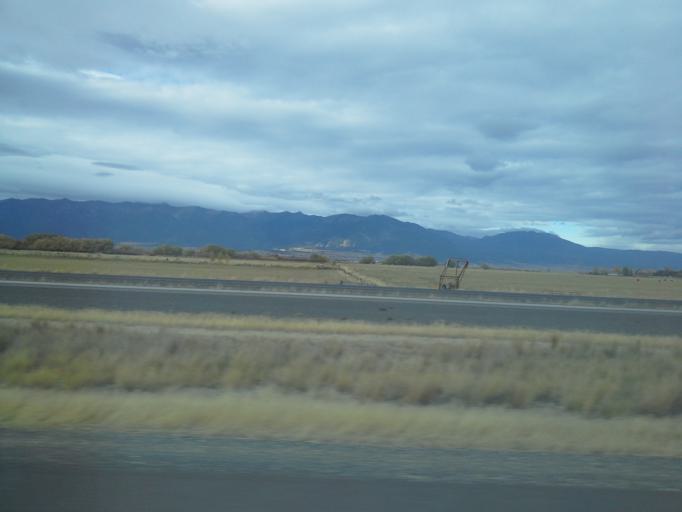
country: US
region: Oregon
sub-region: Baker County
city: Baker City
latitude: 44.8540
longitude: -117.8162
